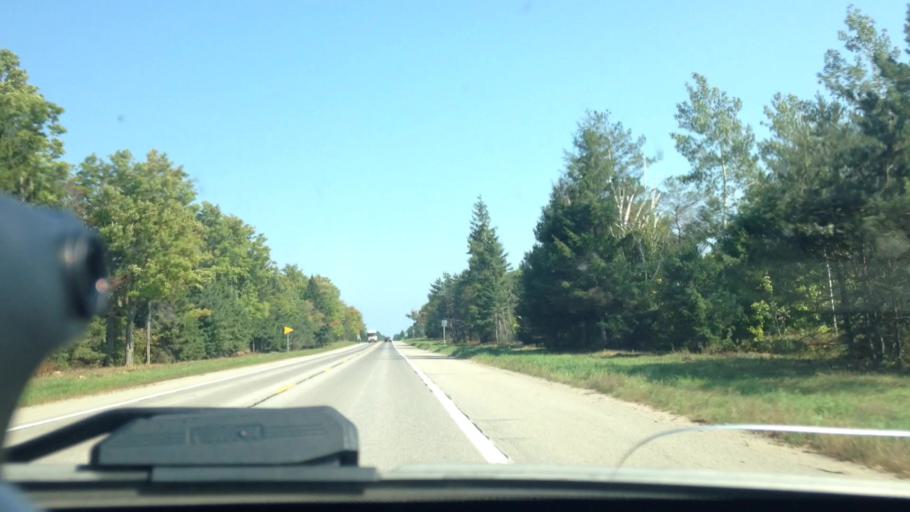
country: US
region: Michigan
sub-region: Luce County
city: Newberry
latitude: 46.3034
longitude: -85.4665
